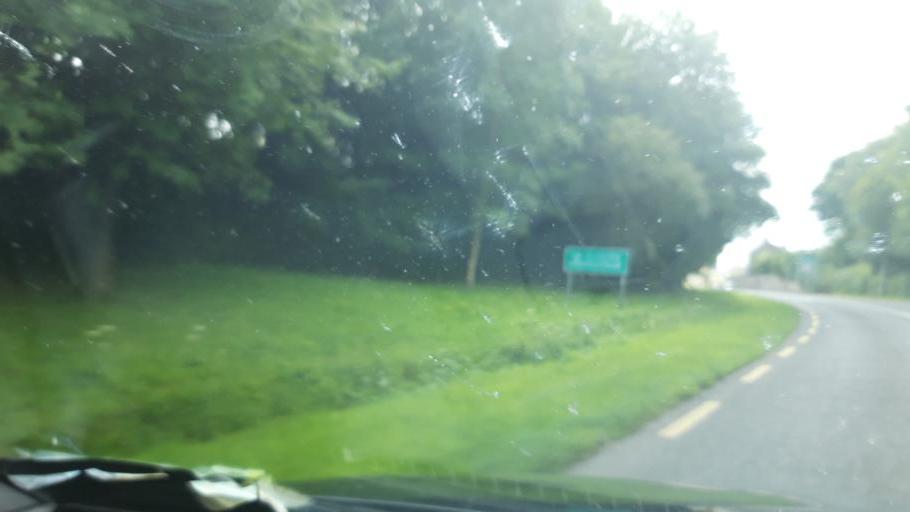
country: IE
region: Leinster
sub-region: Kilkenny
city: Callan
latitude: 52.4632
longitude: -7.4631
